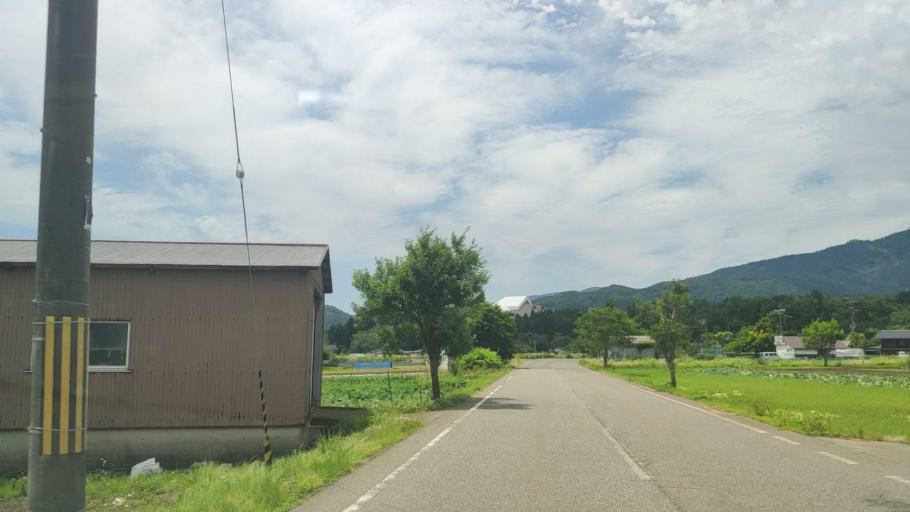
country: JP
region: Hyogo
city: Toyooka
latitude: 35.5014
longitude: 134.6904
